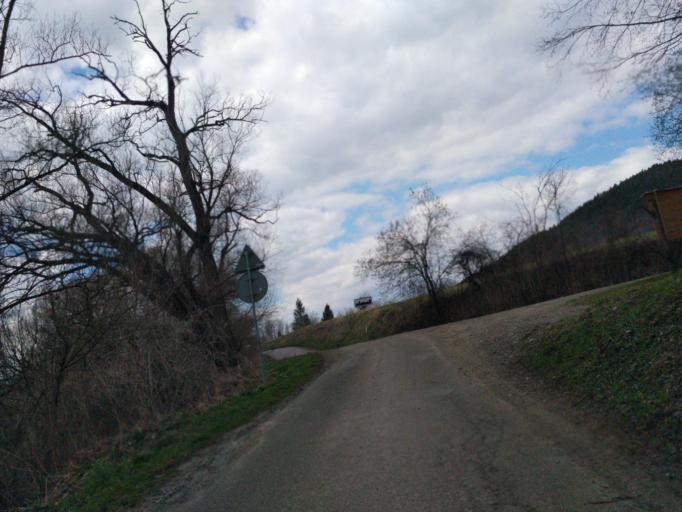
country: PL
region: Subcarpathian Voivodeship
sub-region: Powiat sanocki
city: Tyrawa Woloska
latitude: 49.6637
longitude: 22.2939
